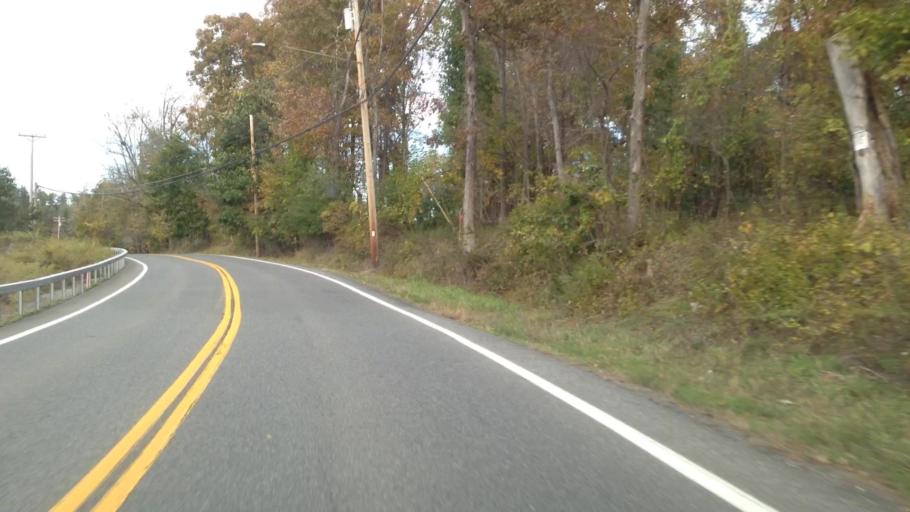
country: US
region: New York
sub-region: Ulster County
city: Tillson
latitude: 41.8466
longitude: -74.0371
